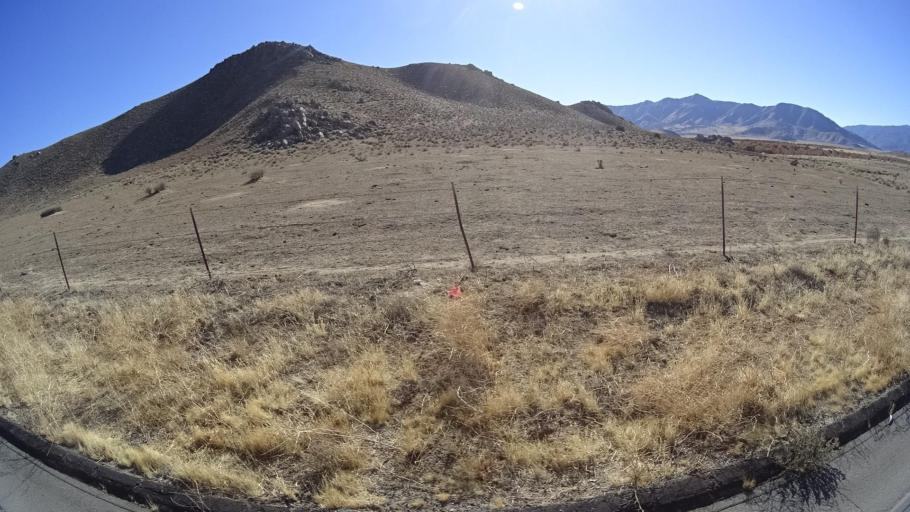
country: US
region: California
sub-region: Kern County
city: Weldon
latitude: 35.6793
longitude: -118.3636
